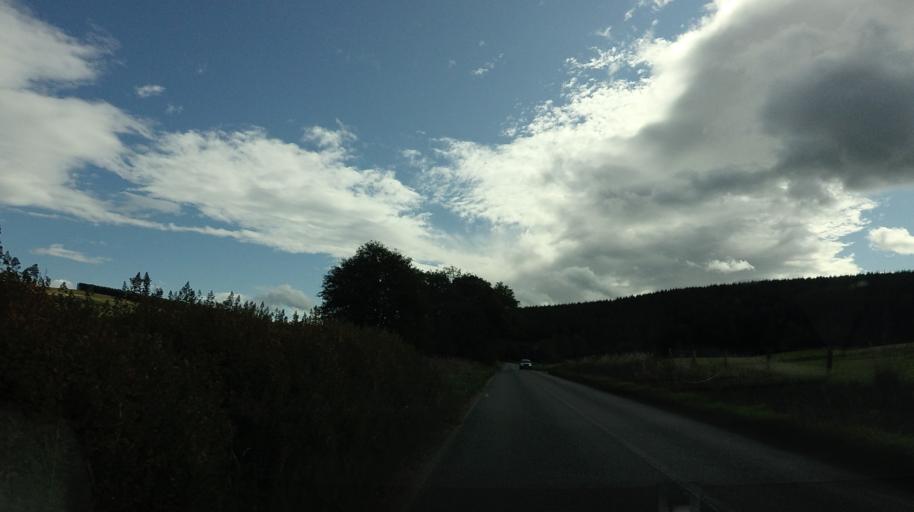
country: GB
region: Scotland
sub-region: Aberdeenshire
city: Torphins
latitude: 57.1266
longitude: -2.6776
